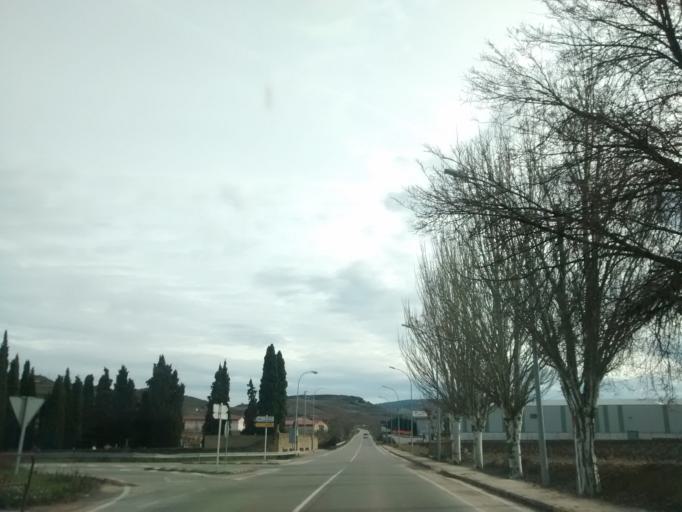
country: ES
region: La Rioja
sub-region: Provincia de La Rioja
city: Cenicero
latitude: 42.4782
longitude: -2.6345
